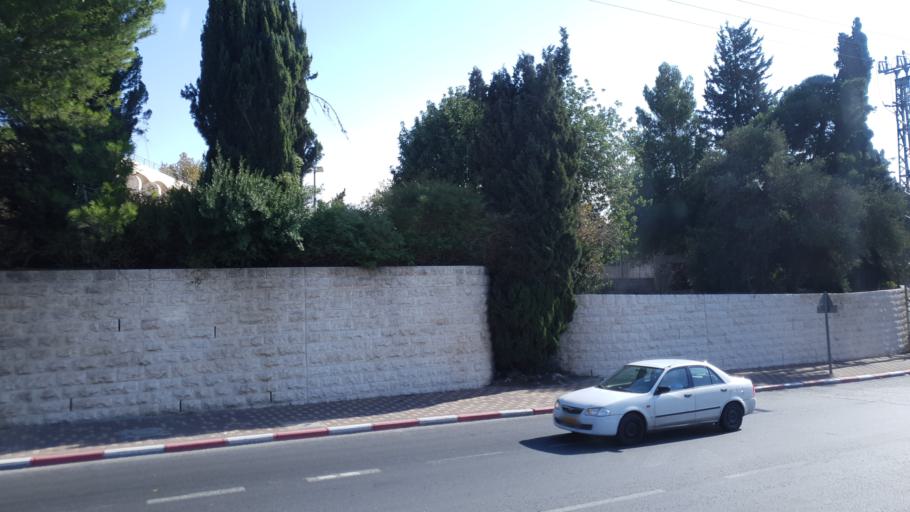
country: PS
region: West Bank
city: East Jerusalem
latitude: 31.7969
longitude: 35.2351
